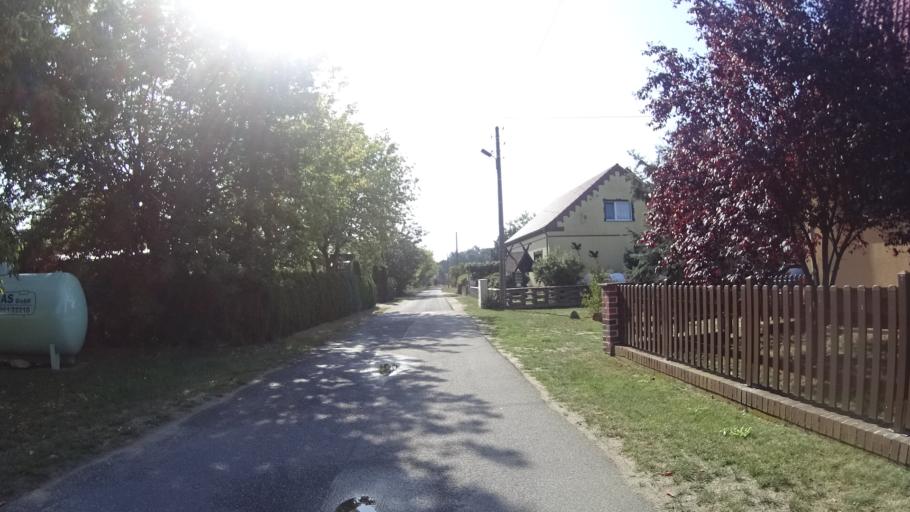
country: DE
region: Brandenburg
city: Neu Zauche
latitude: 51.9151
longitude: 14.0224
